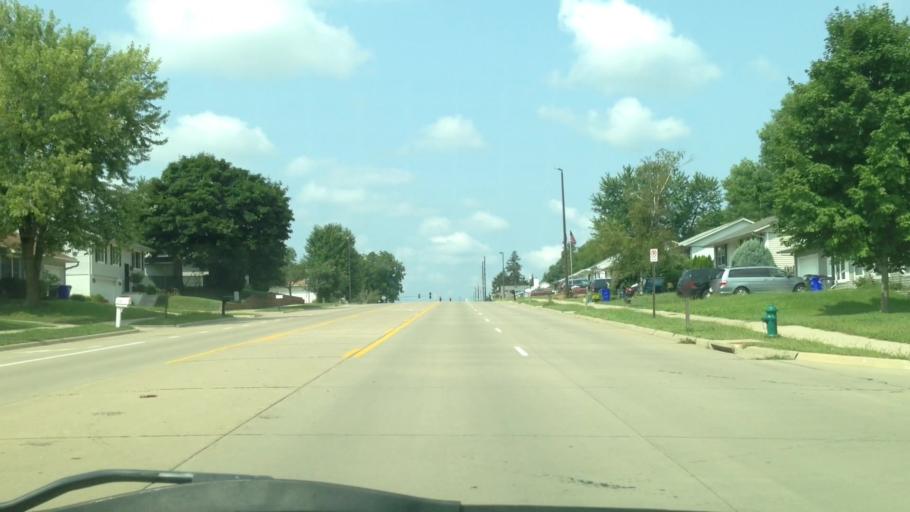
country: US
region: Iowa
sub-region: Linn County
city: Fairfax
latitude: 41.9457
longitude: -91.7119
